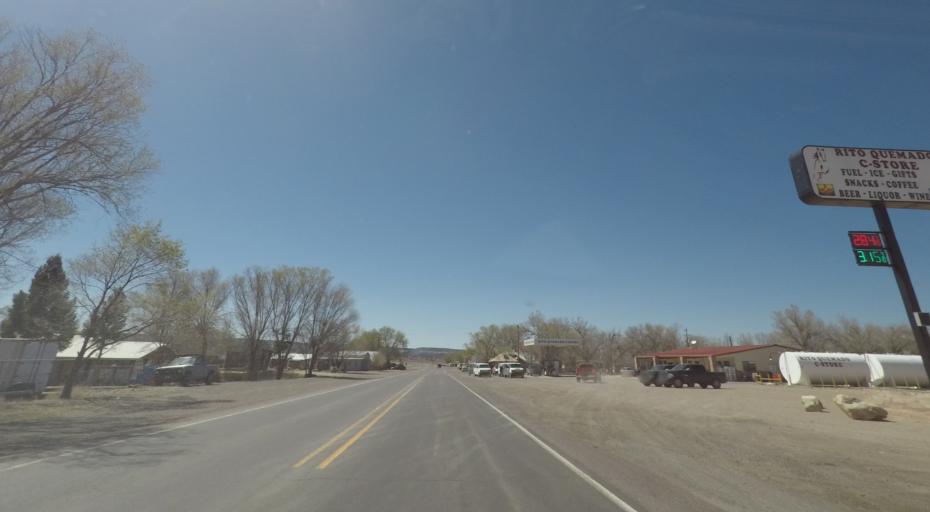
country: US
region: New Mexico
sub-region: Catron County
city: Reserve
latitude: 34.3431
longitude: -108.4960
